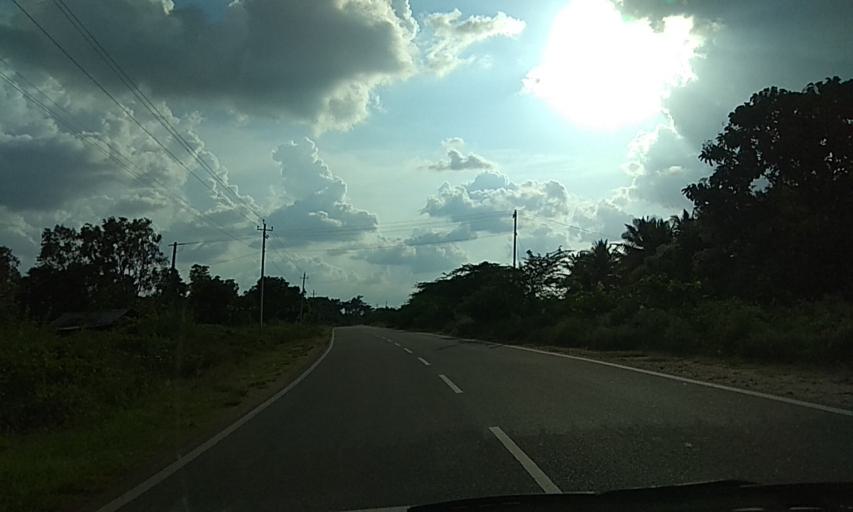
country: IN
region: Karnataka
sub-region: Chamrajnagar
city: Gundlupet
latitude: 11.8135
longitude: 76.7790
